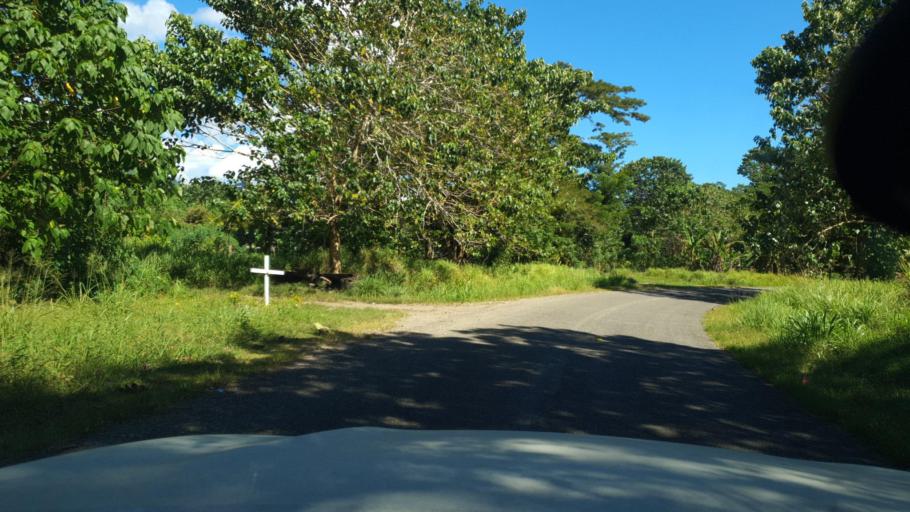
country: SB
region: Guadalcanal
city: Honiara
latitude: -9.2910
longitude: 159.7498
